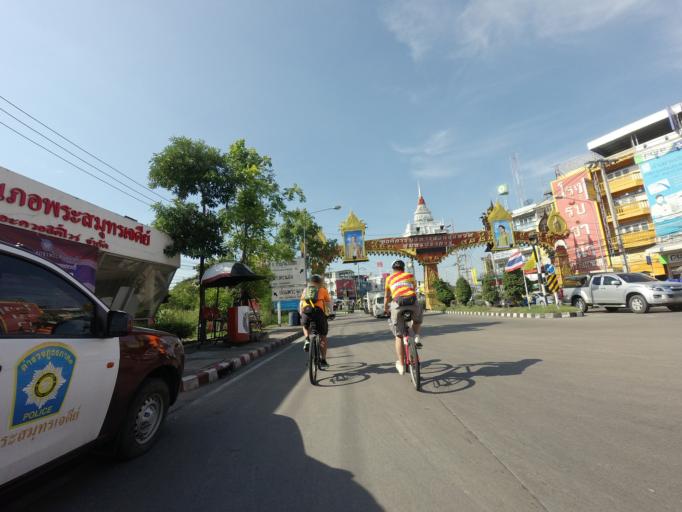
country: TH
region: Samut Prakan
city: Phra Samut Chedi
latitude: 13.5947
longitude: 100.5802
